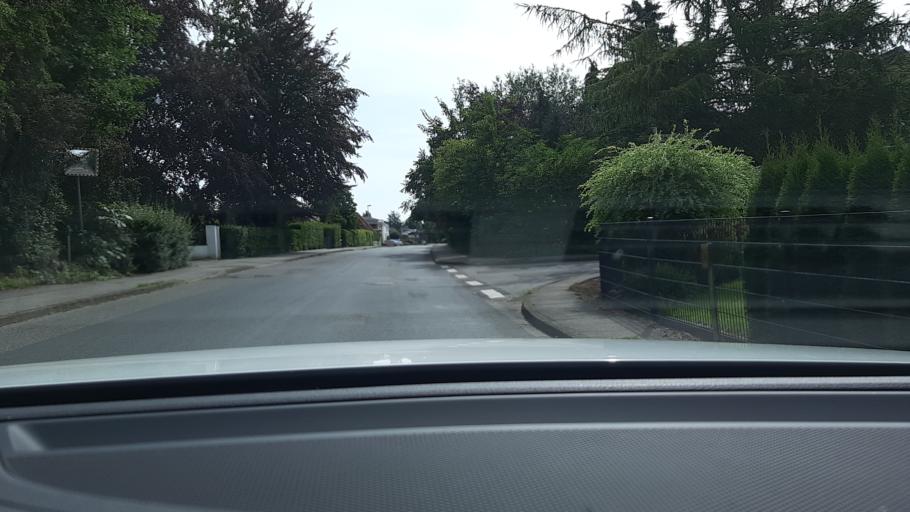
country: DE
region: Schleswig-Holstein
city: Zarpen
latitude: 53.8752
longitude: 10.5191
